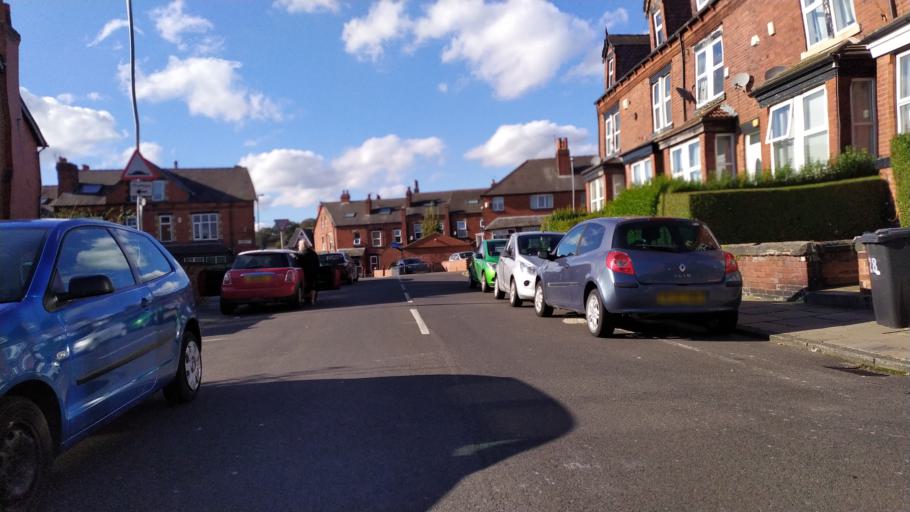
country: GB
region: England
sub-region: City and Borough of Leeds
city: Leeds
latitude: 53.8210
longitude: -1.5840
